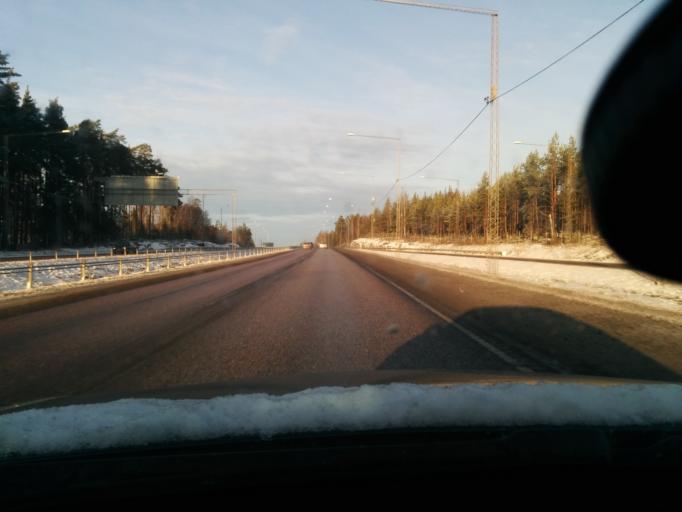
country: SE
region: Stockholm
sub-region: Sigtuna Kommun
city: Rosersberg
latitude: 59.6225
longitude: 17.9012
